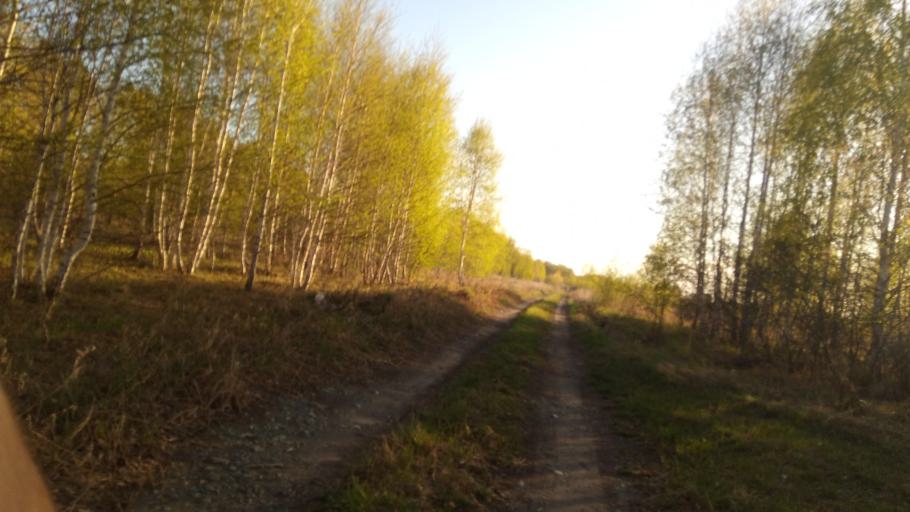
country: RU
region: Chelyabinsk
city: Timiryazevskiy
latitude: 54.9901
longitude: 60.8597
